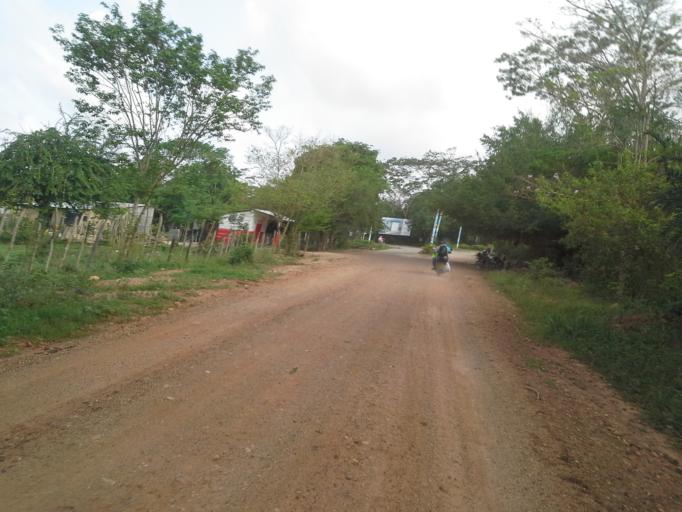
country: CO
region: Cordoba
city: Chima
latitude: 9.1494
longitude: -75.6196
